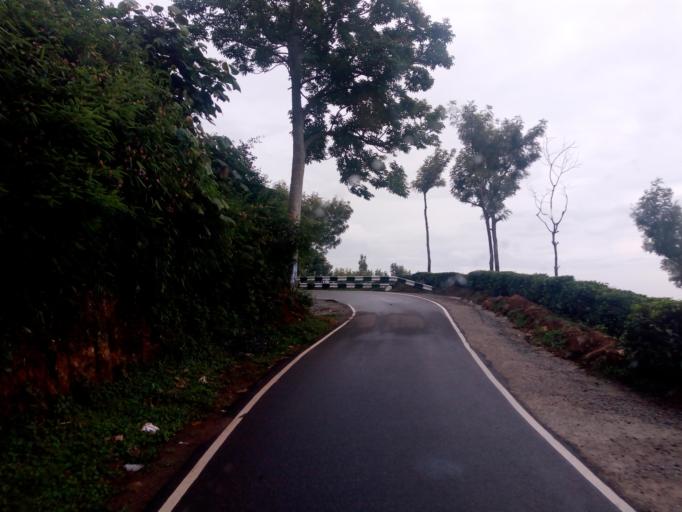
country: IN
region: Tamil Nadu
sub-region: Nilgiri
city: Kotagiri
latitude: 11.3620
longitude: 76.8484
